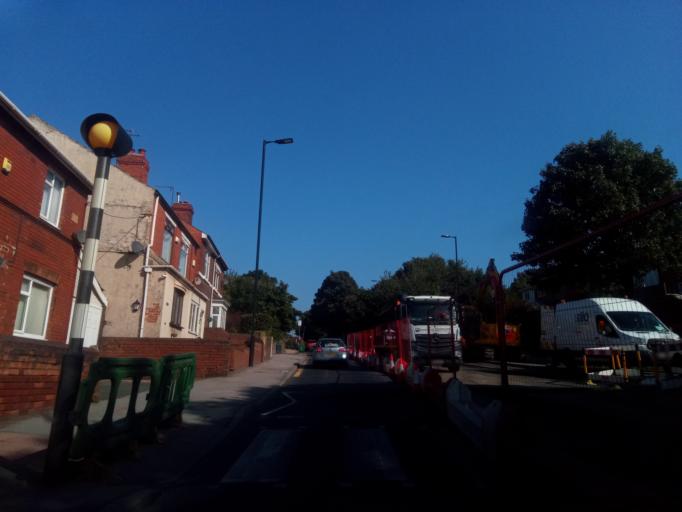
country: GB
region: England
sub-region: Doncaster
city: Mexborough
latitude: 53.4530
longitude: -1.2975
